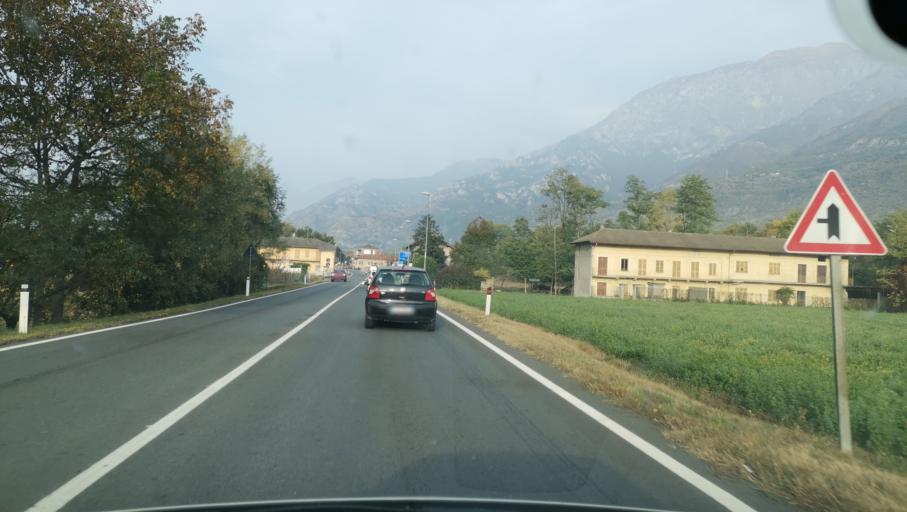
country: IT
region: Piedmont
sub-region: Provincia di Torino
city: San Giorio
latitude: 45.1349
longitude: 7.1812
